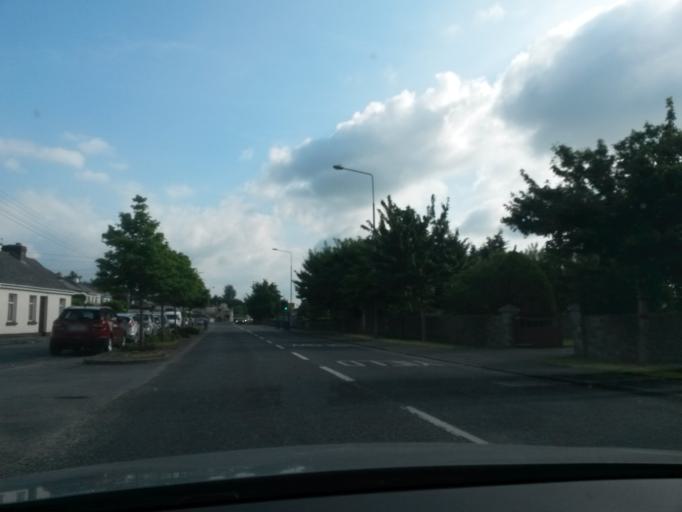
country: IE
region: Munster
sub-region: An Clar
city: Ennis
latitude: 52.8465
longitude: -8.9738
